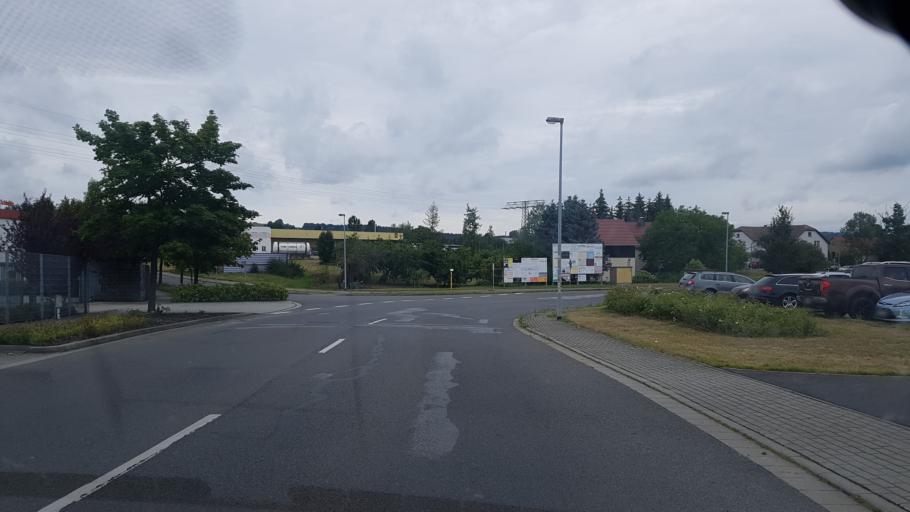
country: DE
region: Saxony
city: Ohorn
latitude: 51.1592
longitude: 14.0524
